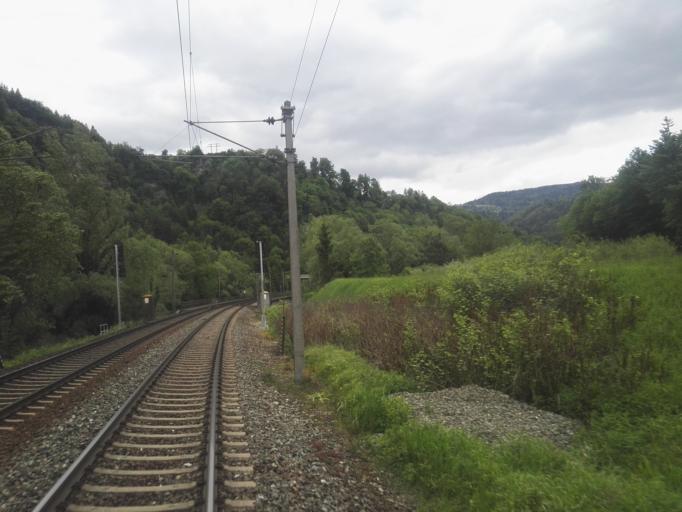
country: AT
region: Styria
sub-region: Politischer Bezirk Graz-Umgebung
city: Peggau
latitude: 47.2194
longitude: 15.3370
